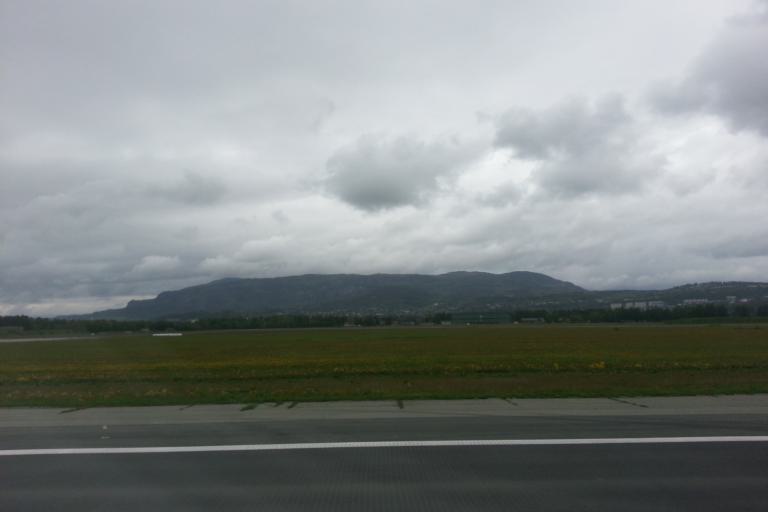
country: NO
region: Nord-Trondelag
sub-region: Stjordal
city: Stjordalshalsen
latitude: 63.4577
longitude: 10.9269
